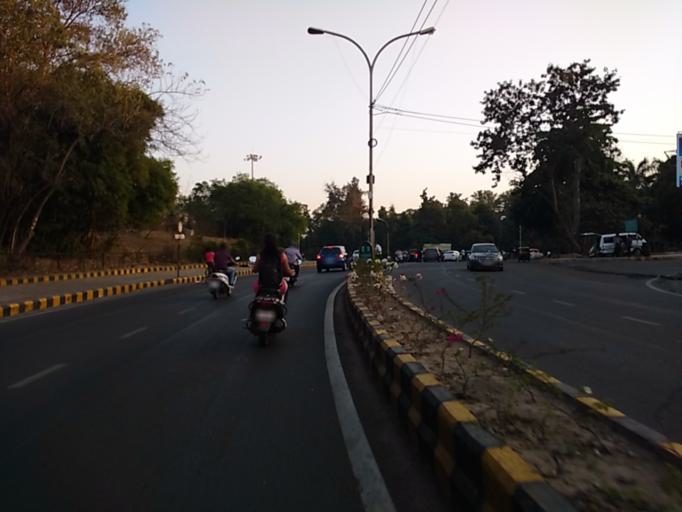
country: IN
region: Maharashtra
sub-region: Nagpur Division
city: Nagpur
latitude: 21.1676
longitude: 79.0701
